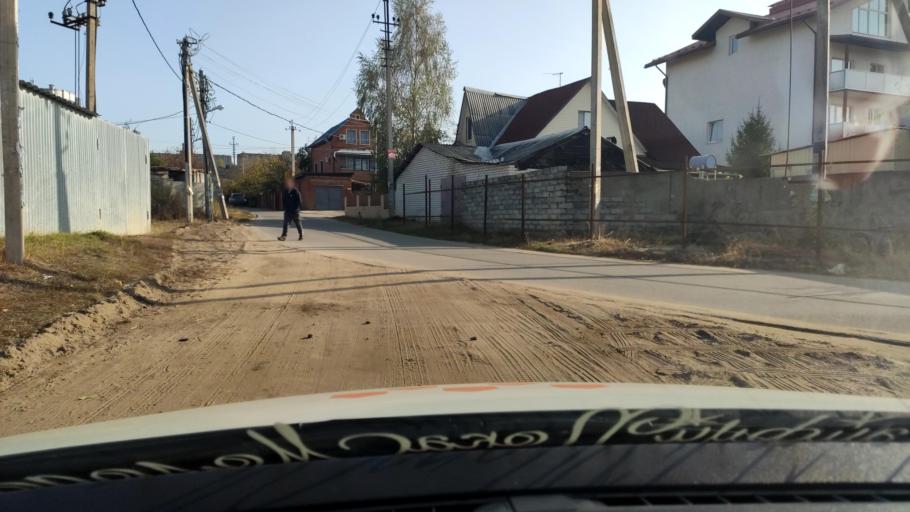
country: RU
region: Voronezj
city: Pridonskoy
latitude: 51.6544
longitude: 39.0957
